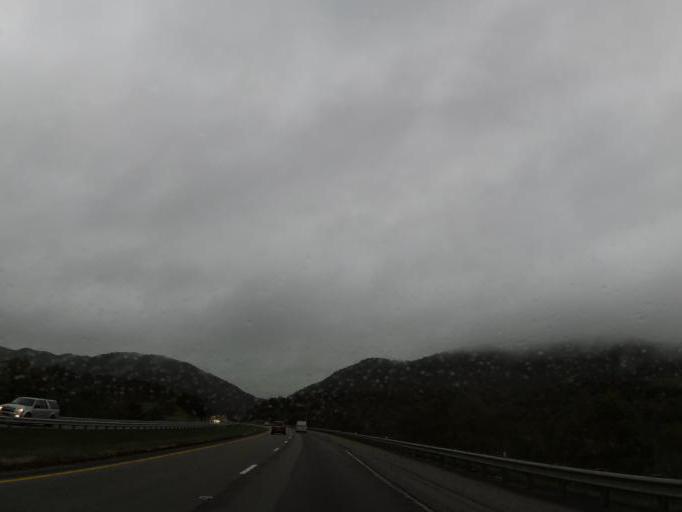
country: US
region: Virginia
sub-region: Wythe County
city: Wytheville
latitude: 37.0052
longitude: -81.0984
